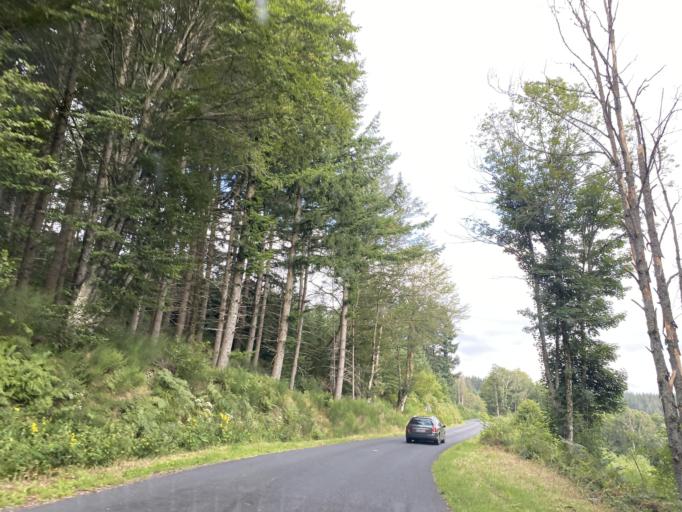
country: FR
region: Auvergne
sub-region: Departement du Puy-de-Dome
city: Celles-sur-Durolle
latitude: 45.7914
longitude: 3.6590
